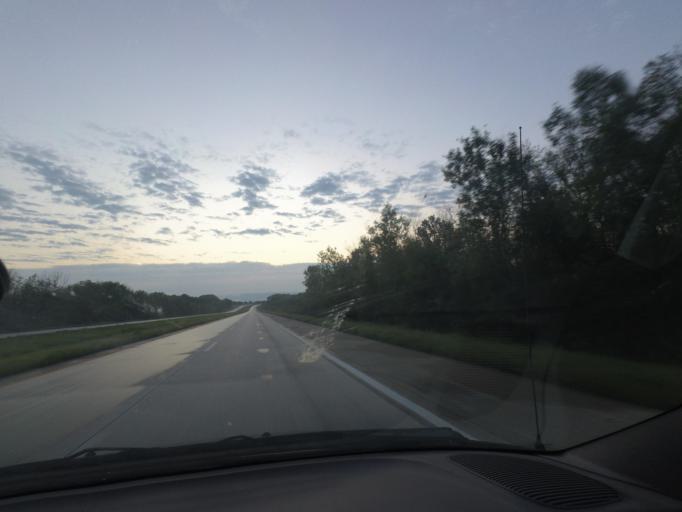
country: US
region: Missouri
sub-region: Macon County
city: Macon
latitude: 39.7595
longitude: -92.5916
